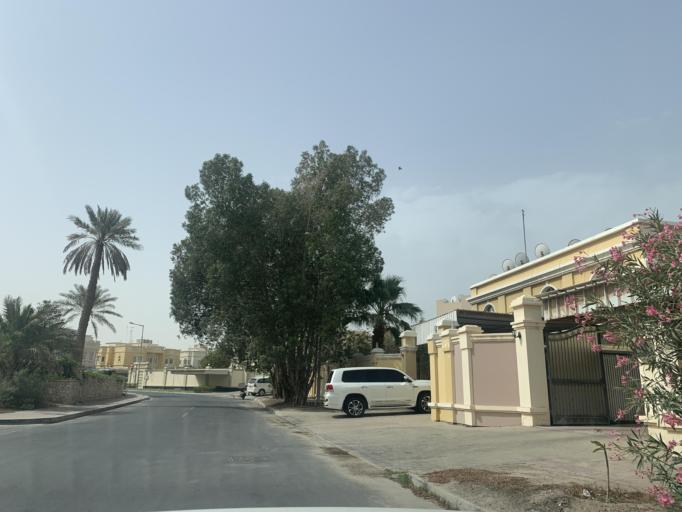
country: BH
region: Central Governorate
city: Madinat Hamad
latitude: 26.1427
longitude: 50.5144
